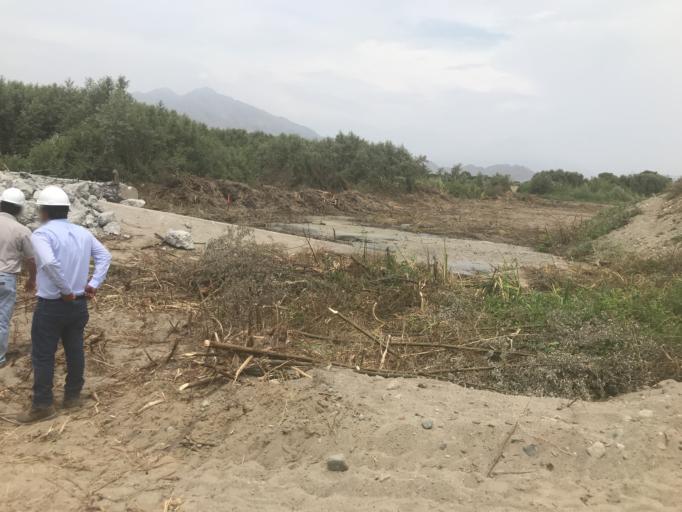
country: PE
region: La Libertad
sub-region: Viru
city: Viru
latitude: -8.4226
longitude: -78.7942
